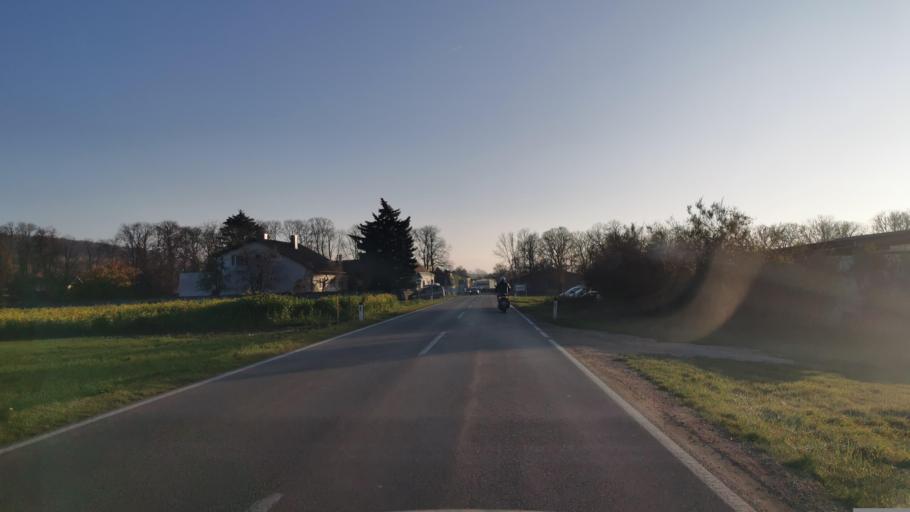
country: AT
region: Lower Austria
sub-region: Politischer Bezirk Korneuburg
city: Stetten
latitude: 48.3837
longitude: 16.3888
